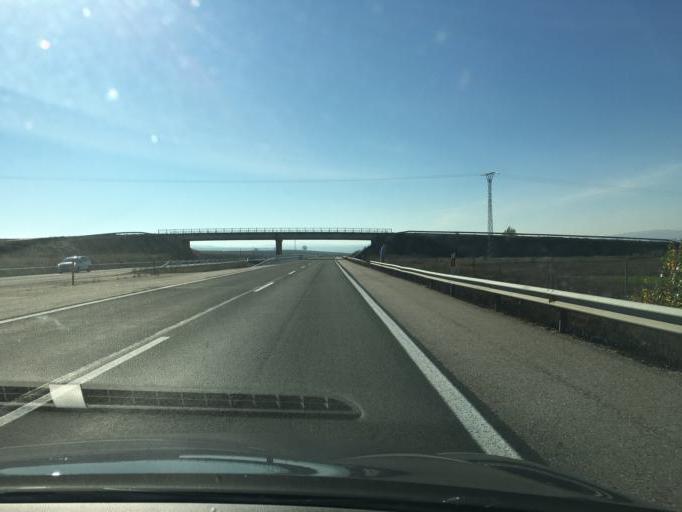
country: ES
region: Castille and Leon
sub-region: Provincia de Burgos
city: Briviesca
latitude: 42.5514
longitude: -3.2849
